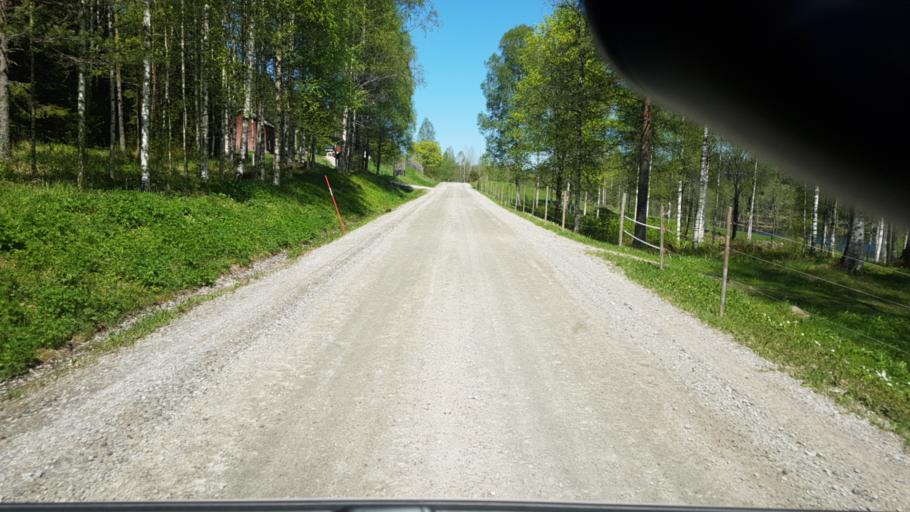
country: SE
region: Vaermland
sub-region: Arvika Kommun
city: Arvika
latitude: 59.8284
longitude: 12.7470
